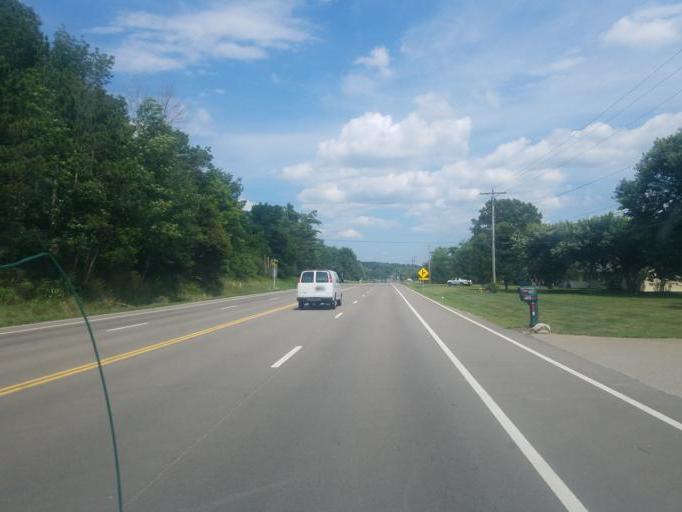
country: US
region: Ohio
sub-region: Muskingum County
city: Zanesville
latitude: 39.9540
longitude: -82.0870
